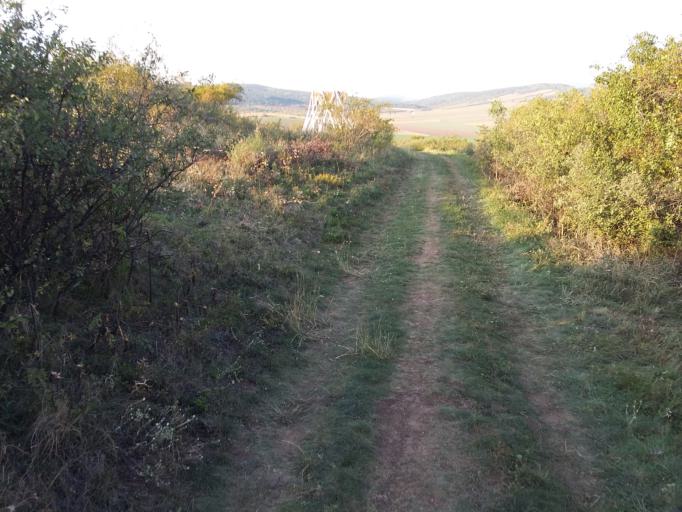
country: HU
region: Borsod-Abauj-Zemplen
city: Bekecs
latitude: 48.1577
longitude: 21.1727
